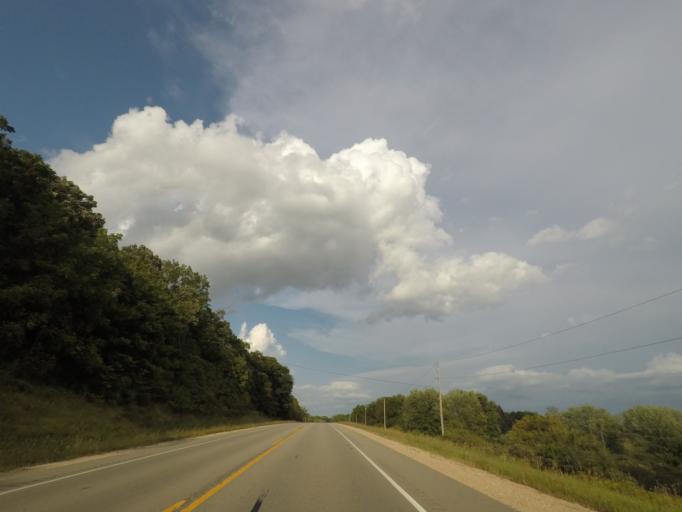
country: US
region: Wisconsin
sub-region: Dane County
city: Waunakee
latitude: 43.1900
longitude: -89.5394
